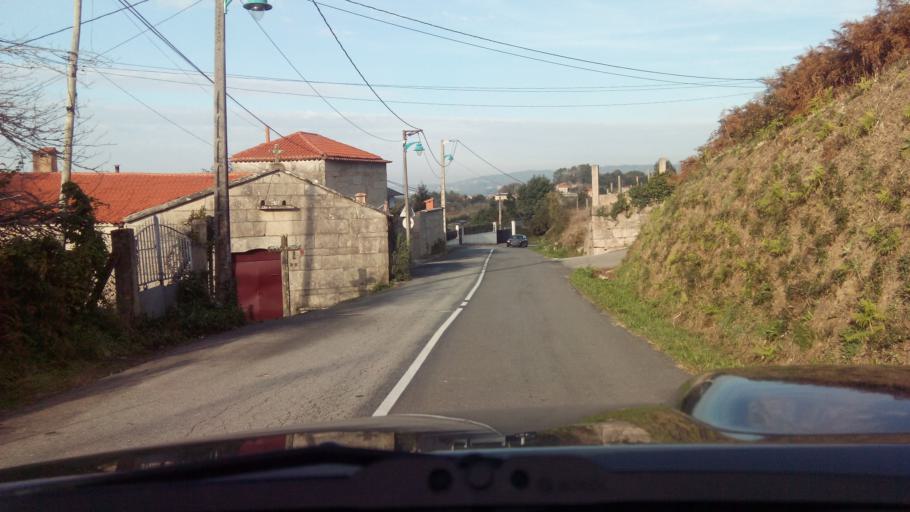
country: ES
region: Galicia
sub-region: Provincia de Pontevedra
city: Marin
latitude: 42.3654
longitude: -8.7185
